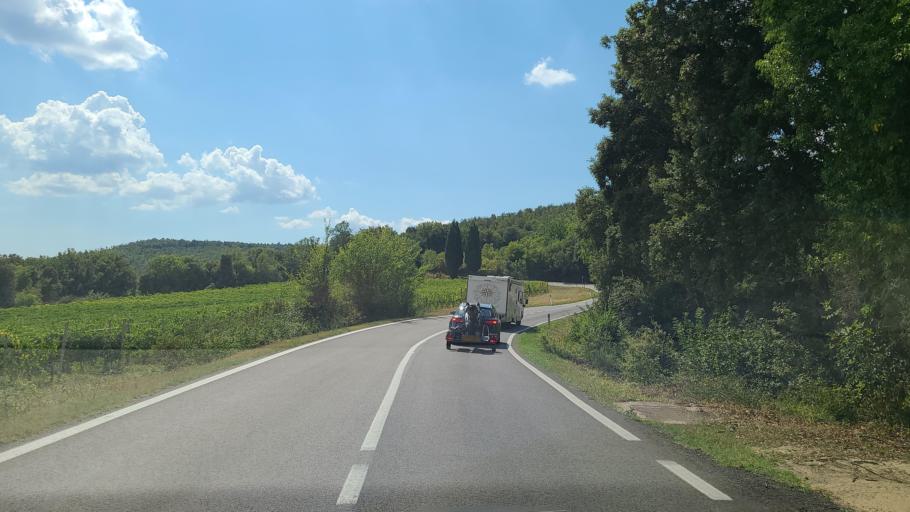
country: IT
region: Tuscany
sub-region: Provincia di Siena
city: Casole d'Elsa
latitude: 43.4028
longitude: 11.0051
